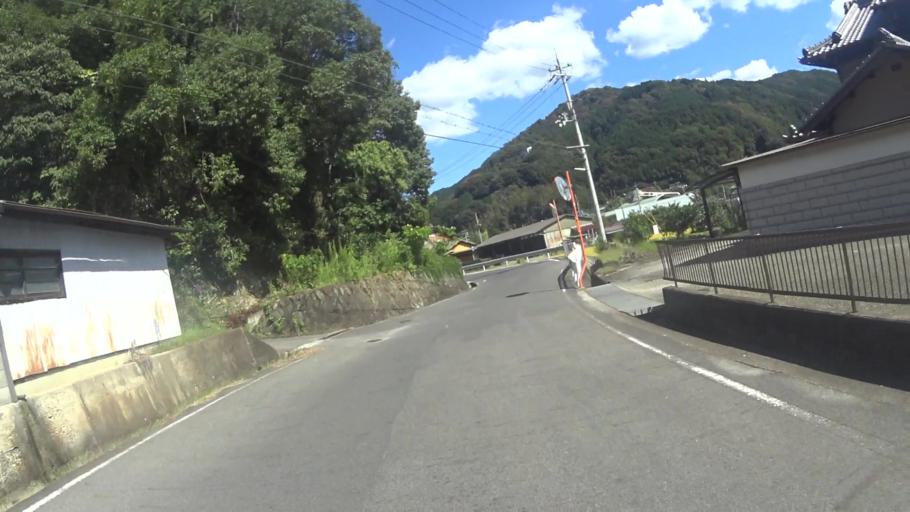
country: JP
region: Nara
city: Nara-shi
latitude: 34.7580
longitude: 135.9315
